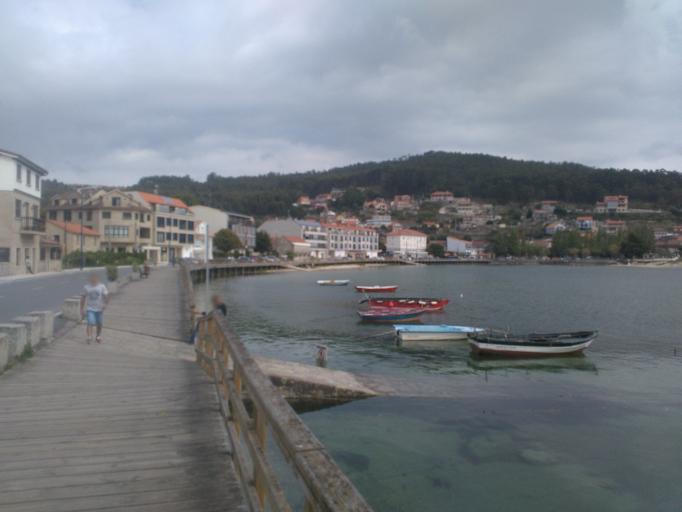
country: ES
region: Galicia
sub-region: Provincia de Pontevedra
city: Cangas
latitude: 42.2806
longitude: -8.8191
